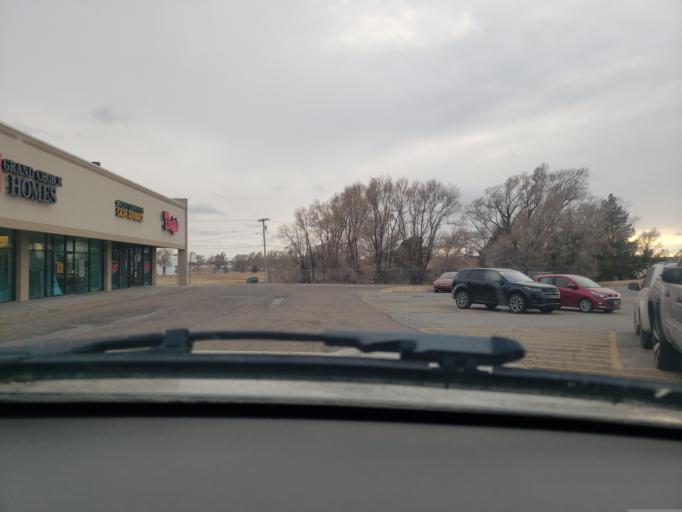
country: US
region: Kansas
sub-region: Finney County
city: Garden City
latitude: 37.9756
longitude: -100.8433
